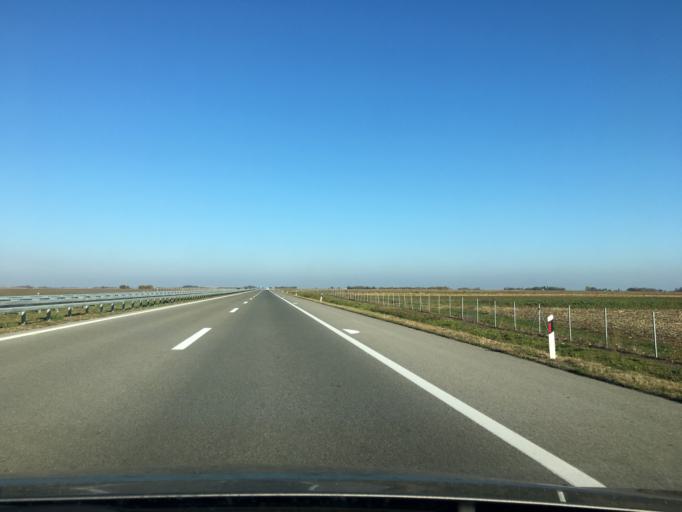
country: RS
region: Autonomna Pokrajina Vojvodina
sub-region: Severnobacki Okrug
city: Mali Igos
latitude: 45.7638
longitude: 19.7013
